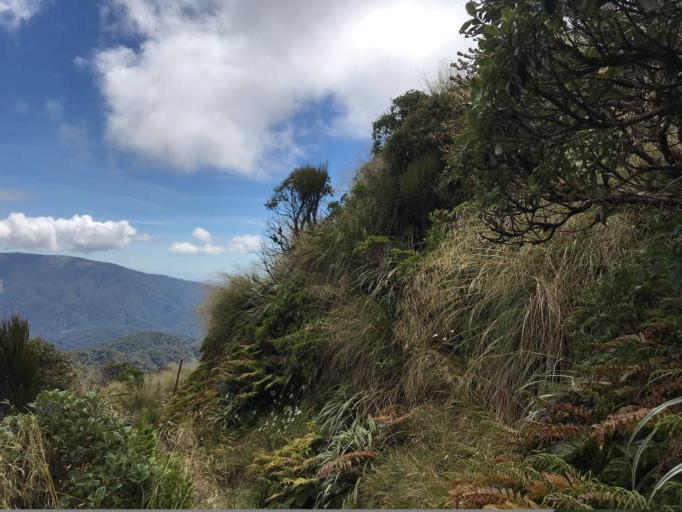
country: NZ
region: Wellington
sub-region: Kapiti Coast District
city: Otaki
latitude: -40.9113
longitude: 175.2616
